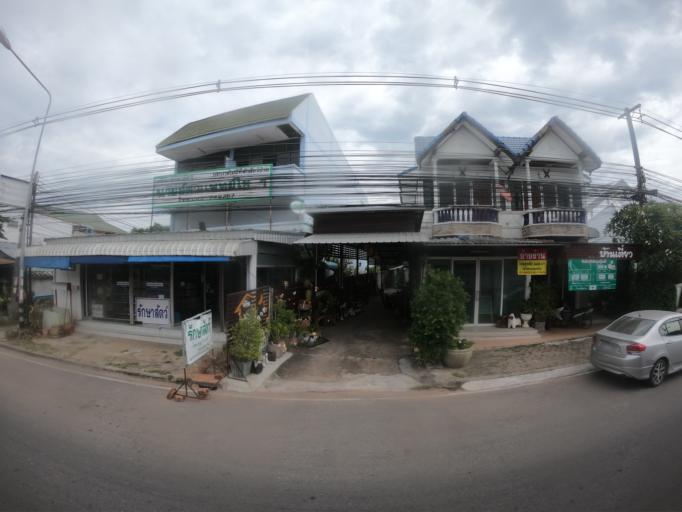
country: TH
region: Maha Sarakham
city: Maha Sarakham
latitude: 16.1967
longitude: 103.2935
